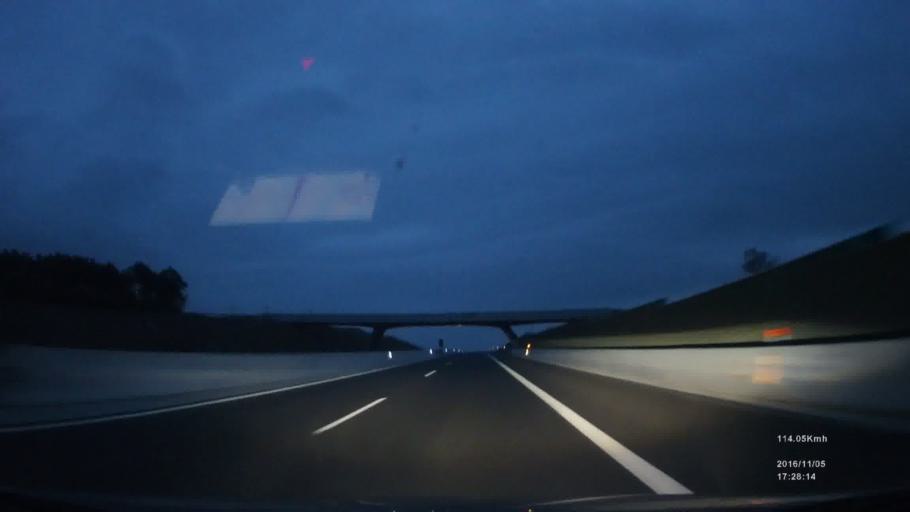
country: SK
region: Kosicky
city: Spisska Nova Ves
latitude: 49.0065
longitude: 20.4689
